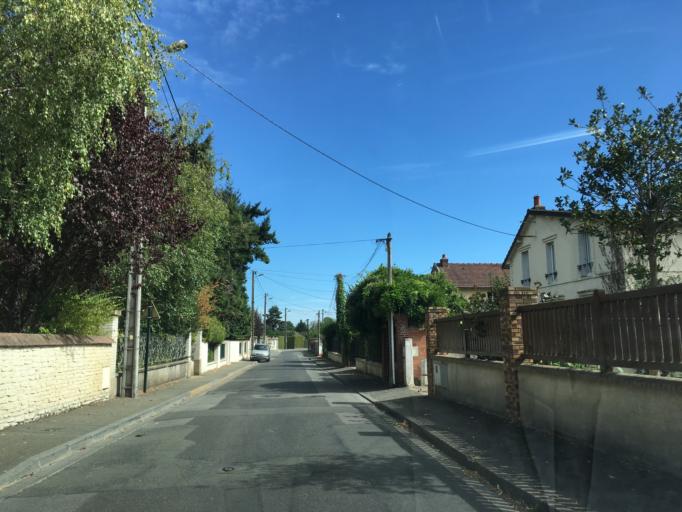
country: FR
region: Haute-Normandie
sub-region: Departement de l'Eure
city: Vernon
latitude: 49.0907
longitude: 1.4614
